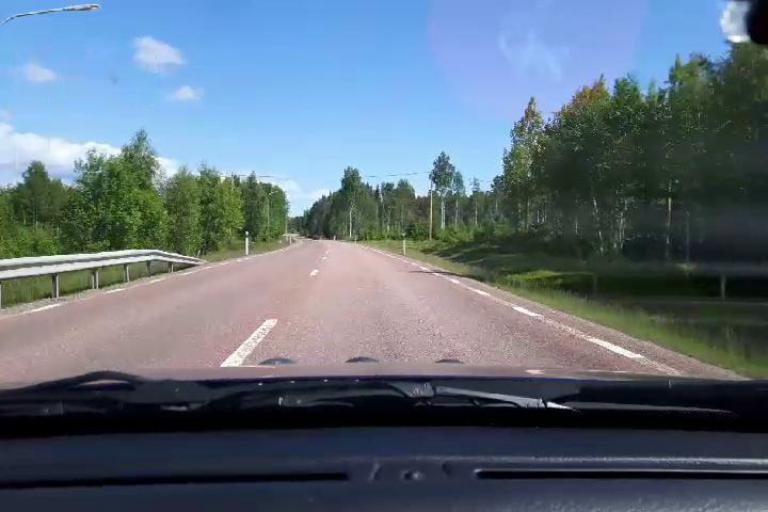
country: SE
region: Gaevleborg
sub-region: Hudiksvalls Kommun
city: Delsbo
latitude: 61.8018
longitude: 16.4785
